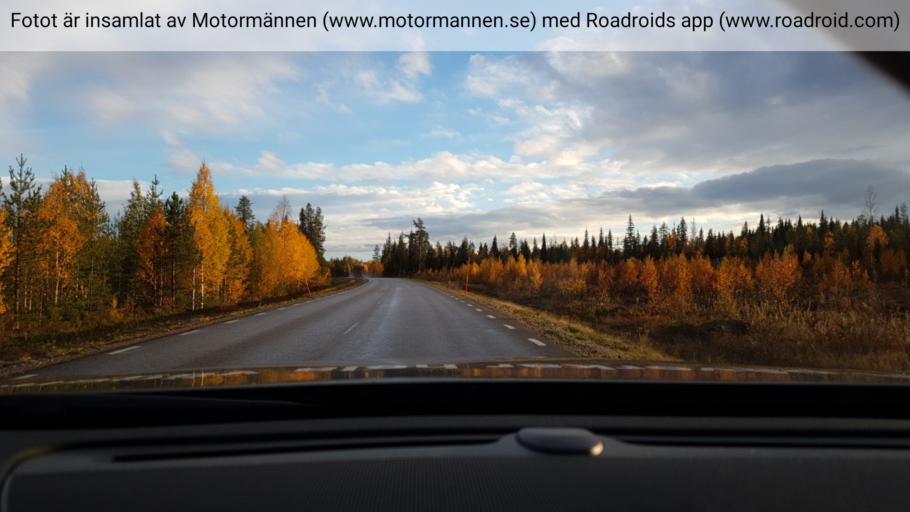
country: SE
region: Norrbotten
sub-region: Overkalix Kommun
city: OEverkalix
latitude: 66.7295
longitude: 22.6663
